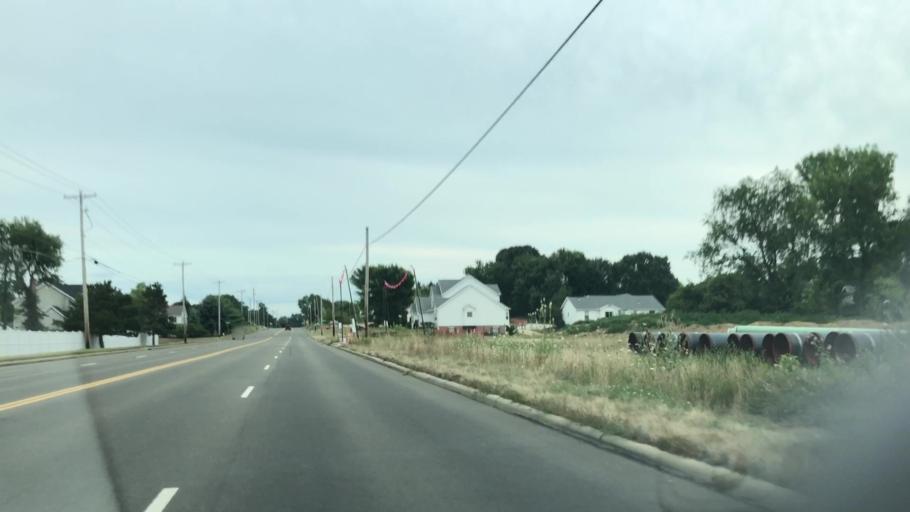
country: US
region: Ohio
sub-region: Stark County
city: Greentown
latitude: 40.9429
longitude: -81.4038
